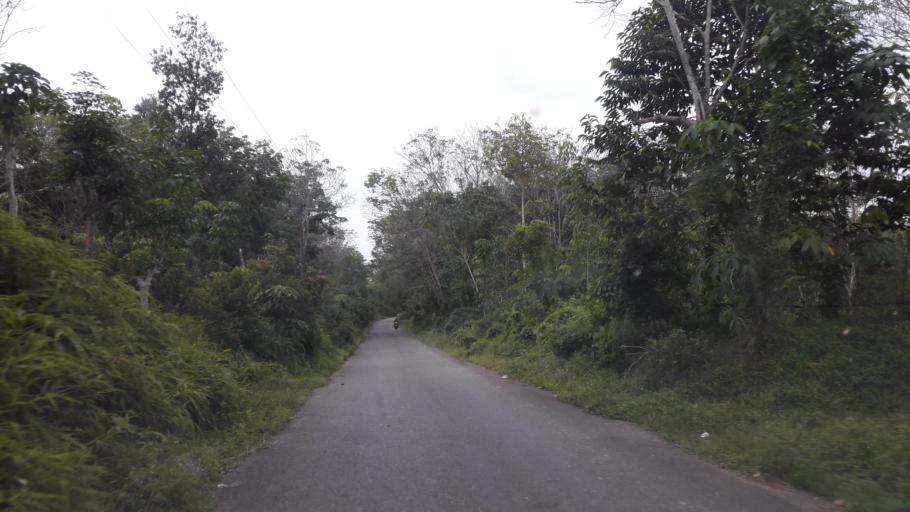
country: ID
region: South Sumatra
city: Gunungmenang
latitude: -3.1222
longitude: 104.1157
